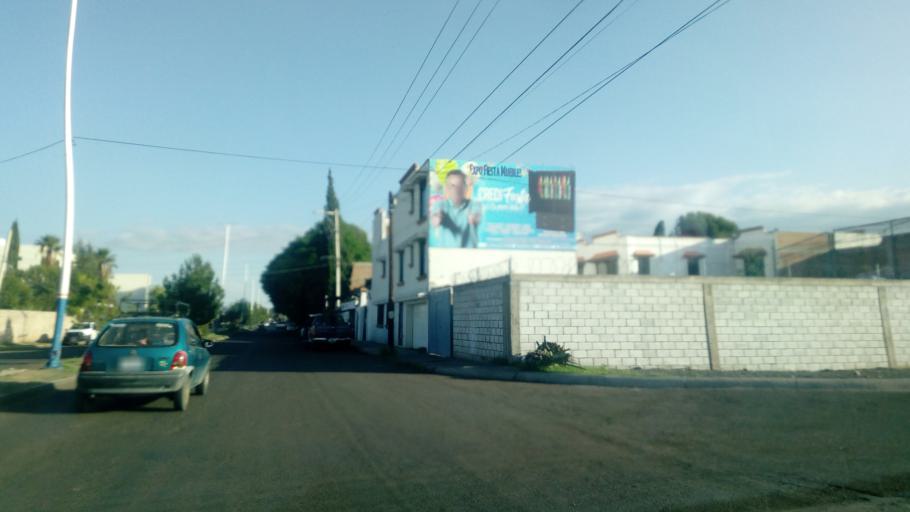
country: MX
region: Durango
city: Victoria de Durango
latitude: 24.0417
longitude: -104.6107
